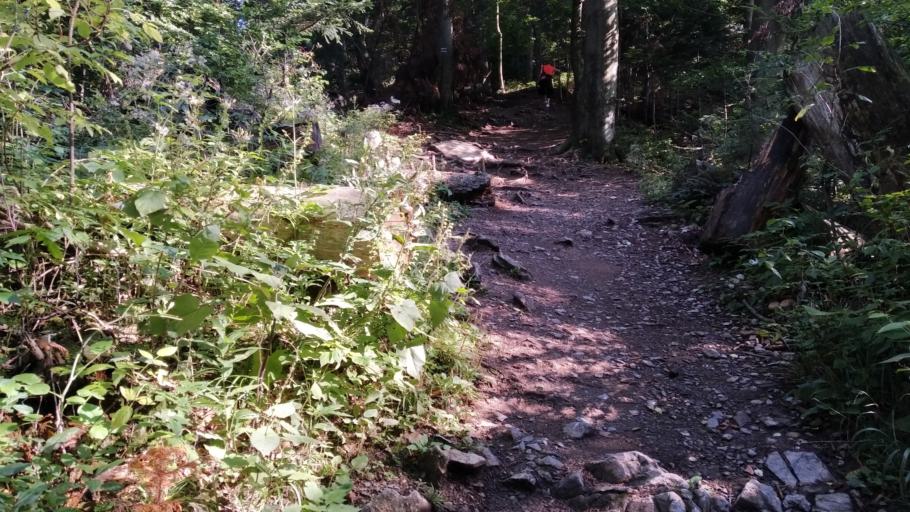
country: PL
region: Lesser Poland Voivodeship
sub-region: Powiat nowotarski
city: Kroscienko nad Dunajcem
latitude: 49.4192
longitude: 20.4395
